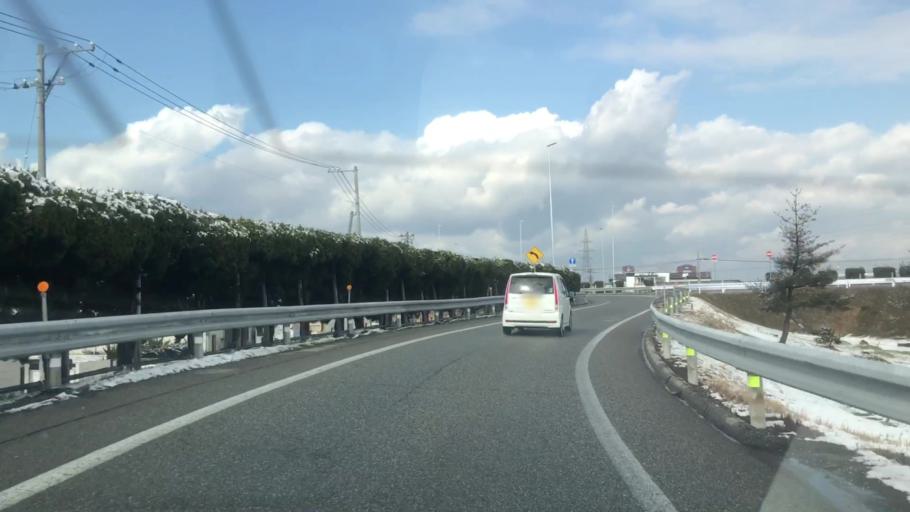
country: JP
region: Toyama
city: Toyama-shi
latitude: 36.6552
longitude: 137.2041
